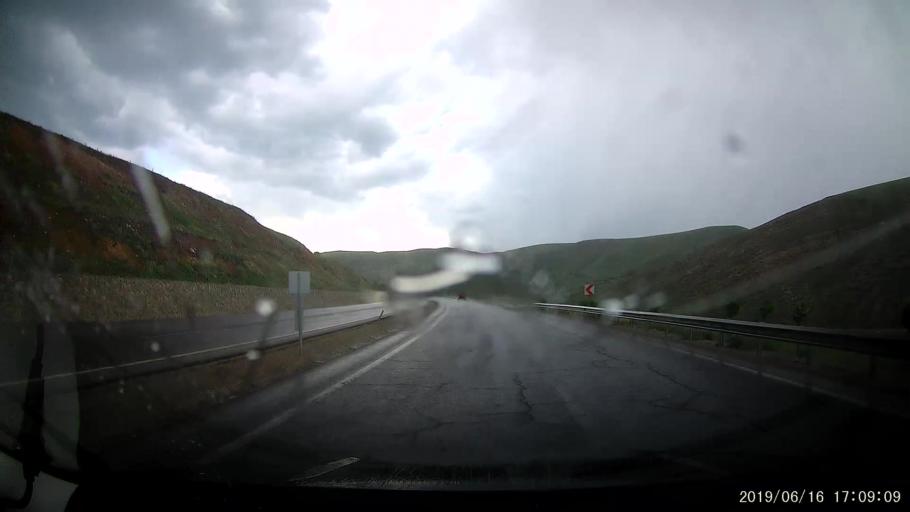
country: TR
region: Erzurum
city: Askale
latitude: 39.8988
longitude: 40.6528
